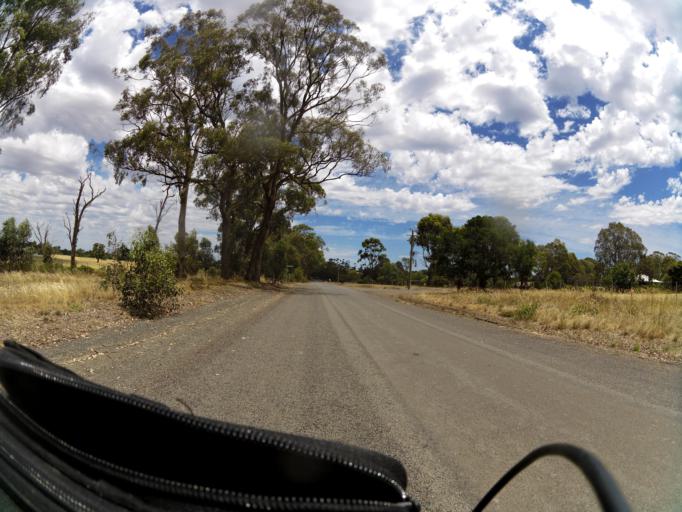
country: AU
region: Victoria
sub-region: Campaspe
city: Kyabram
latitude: -36.7387
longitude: 145.1390
